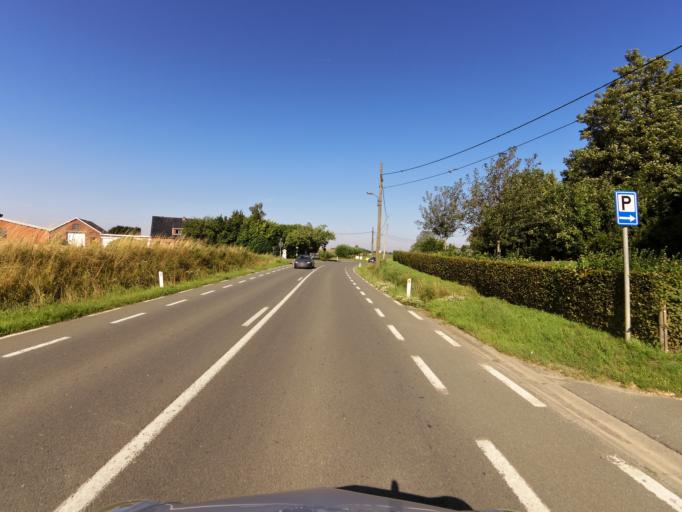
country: BE
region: Flanders
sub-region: Provincie Oost-Vlaanderen
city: Oudenaarde
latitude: 50.8300
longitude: 3.6300
